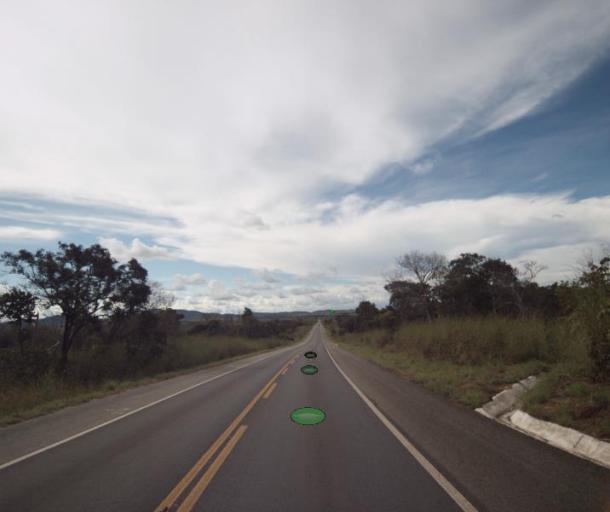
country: BR
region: Goias
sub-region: Barro Alto
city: Barro Alto
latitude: -15.1935
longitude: -48.7035
